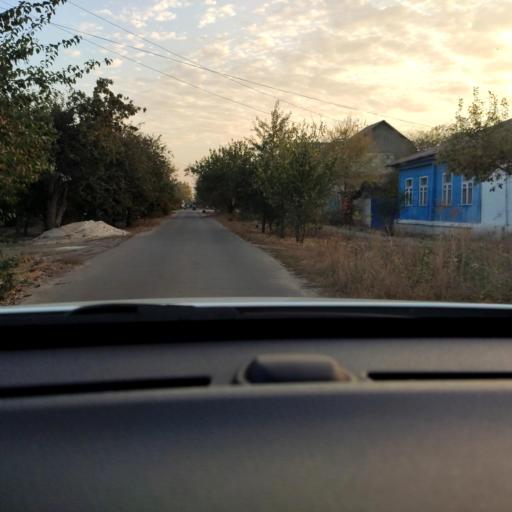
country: RU
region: Voronezj
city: Voronezh
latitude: 51.6650
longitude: 39.2610
